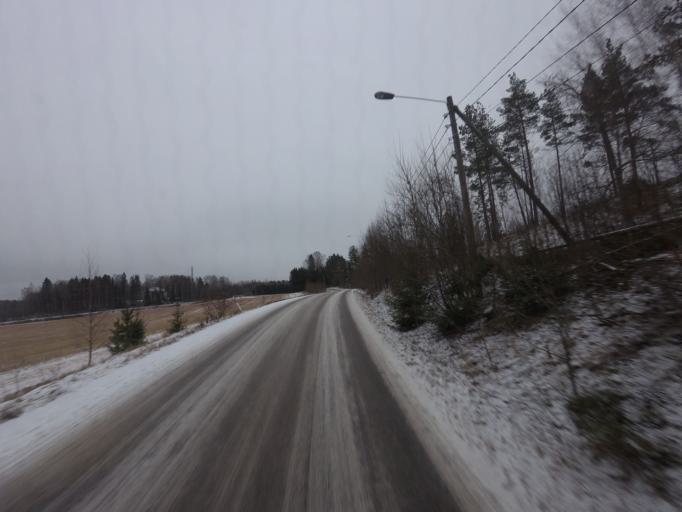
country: FI
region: Uusimaa
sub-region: Helsinki
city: Espoo
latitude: 60.1977
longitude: 24.5637
